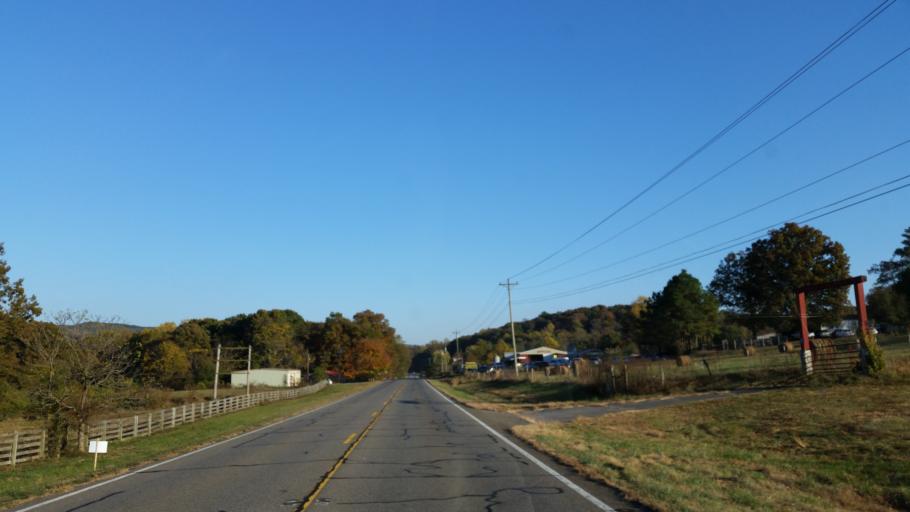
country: US
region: Georgia
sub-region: Gilmer County
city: Ellijay
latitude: 34.6215
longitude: -84.3759
